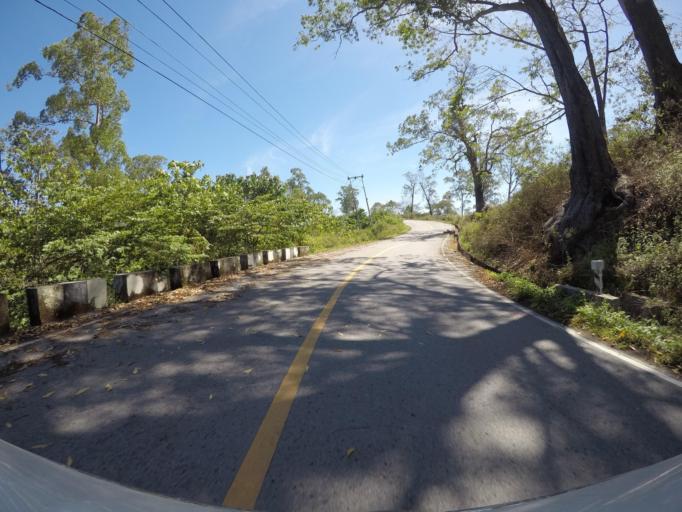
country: TL
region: Manufahi
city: Same
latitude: -8.8938
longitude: 125.9826
